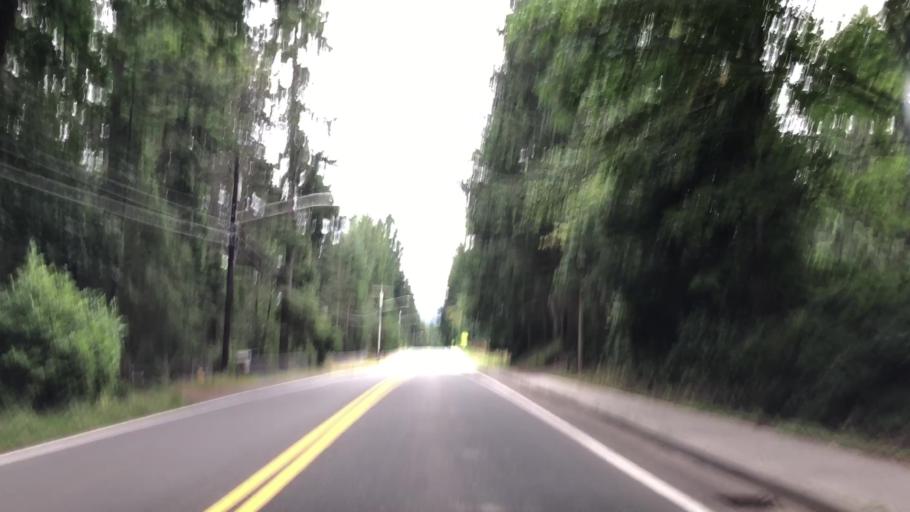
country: US
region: Washington
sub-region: King County
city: Woodinville
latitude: 47.7873
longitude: -122.1568
